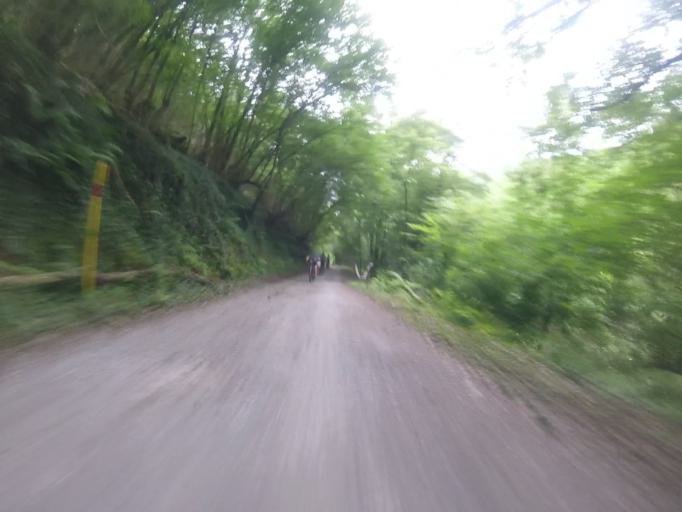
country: ES
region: Navarre
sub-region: Provincia de Navarra
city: Etxalar
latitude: 43.2084
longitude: -1.6640
